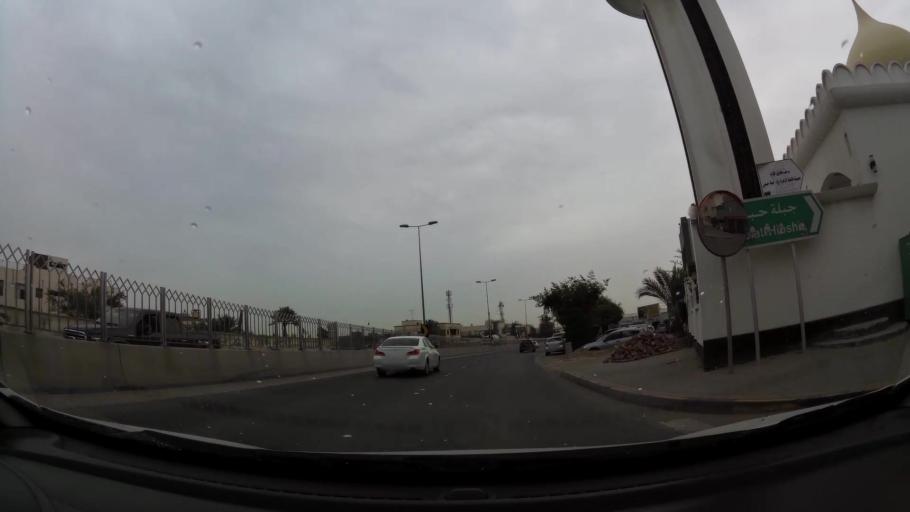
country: BH
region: Manama
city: Jidd Hafs
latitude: 26.2158
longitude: 50.5334
